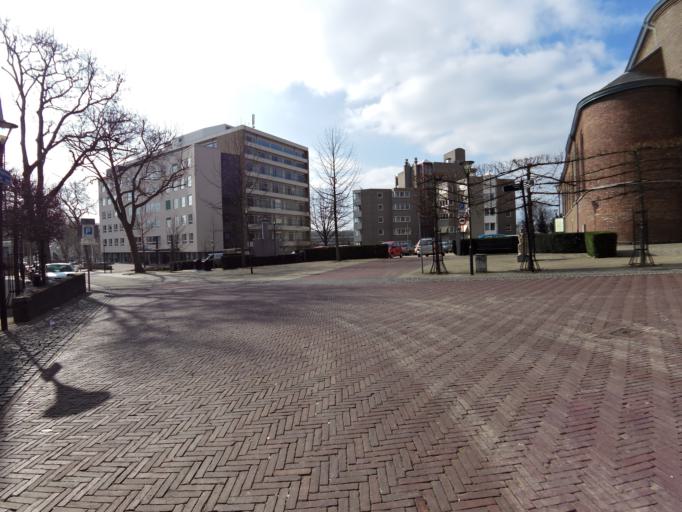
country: NL
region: Limburg
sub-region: Gemeente Kerkrade
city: Kerkrade
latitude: 50.8648
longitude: 6.0612
